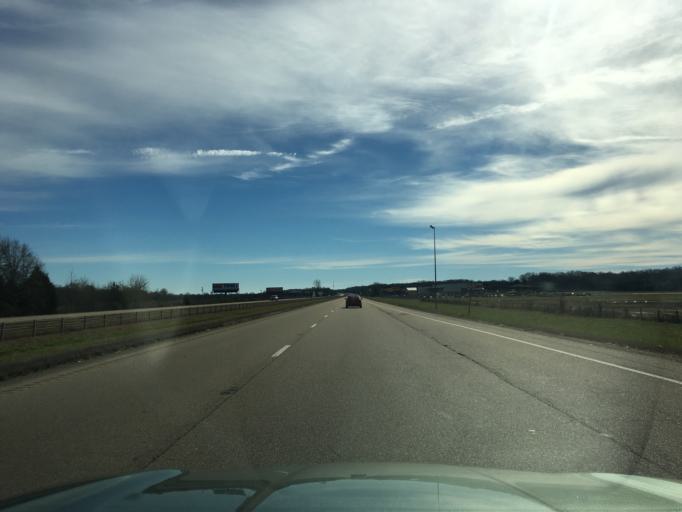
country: US
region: Mississippi
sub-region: Lee County
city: Saltillo
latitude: 34.3502
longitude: -88.8373
